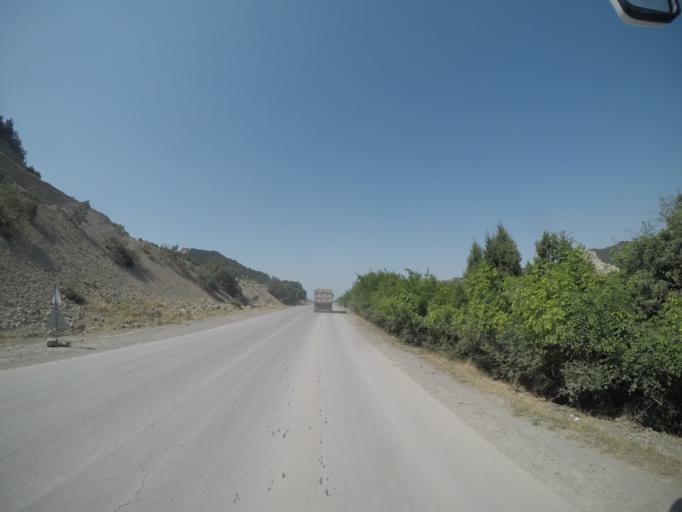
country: AZ
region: Agdas
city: Agdas
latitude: 40.7216
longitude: 47.5630
